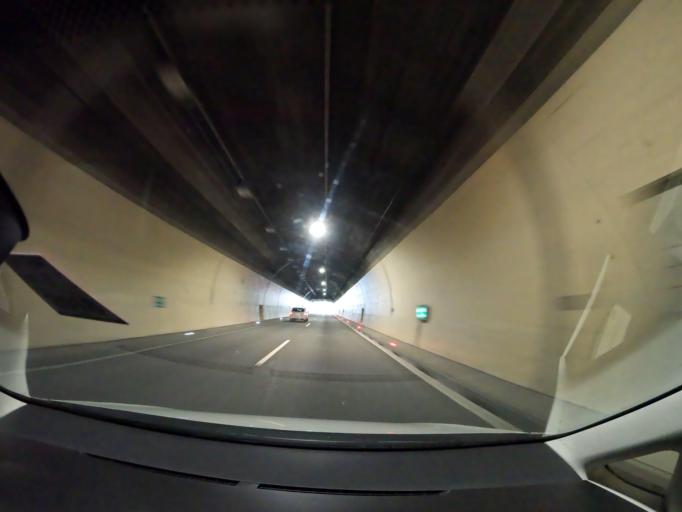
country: AT
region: Carinthia
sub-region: Politischer Bezirk Wolfsberg
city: Bad Sankt Leonhard im Lavanttal
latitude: 46.9178
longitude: 14.8251
